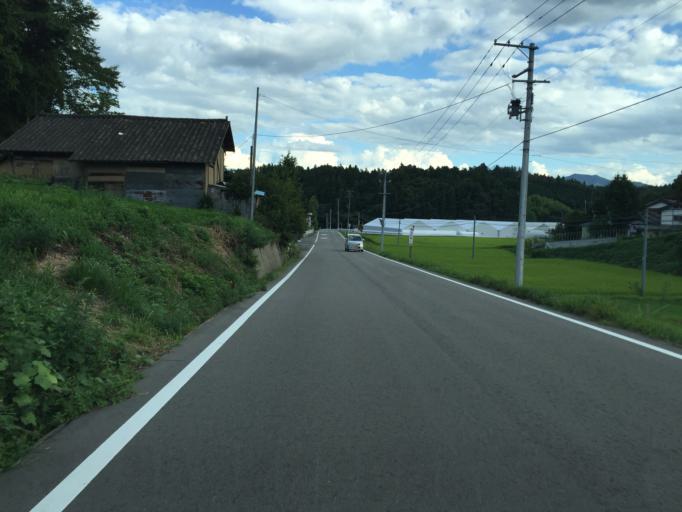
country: JP
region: Fukushima
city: Fukushima-shi
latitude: 37.6867
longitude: 140.5664
